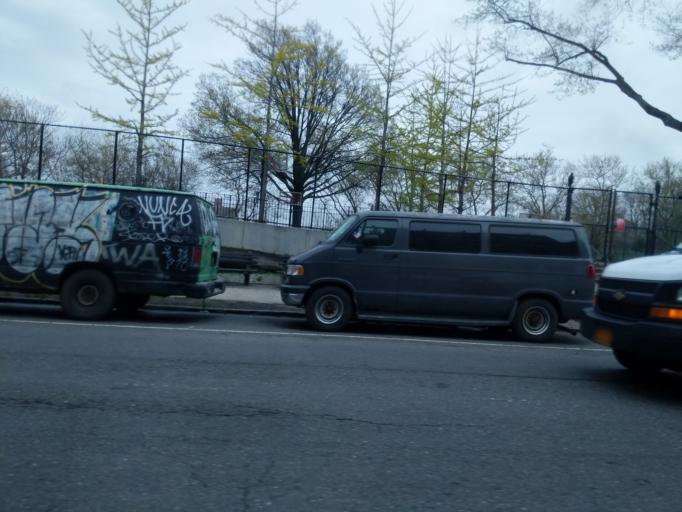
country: US
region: New York
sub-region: New York County
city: Inwood
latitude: 40.8447
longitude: -73.9334
